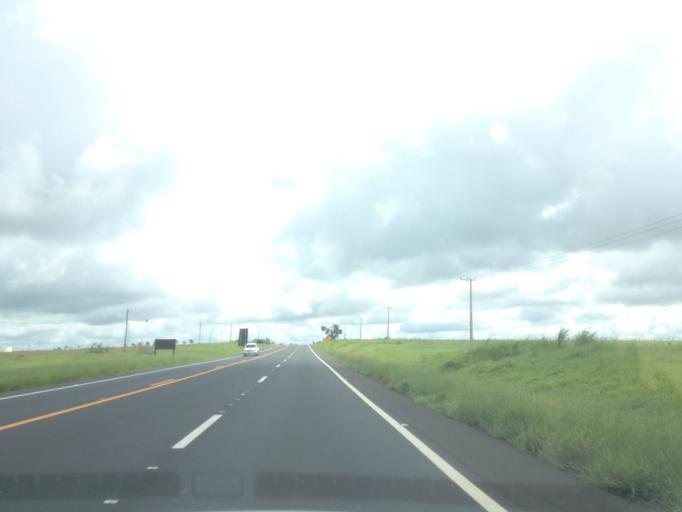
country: BR
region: Sao Paulo
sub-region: Marilia
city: Marilia
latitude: -22.2625
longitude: -49.9946
